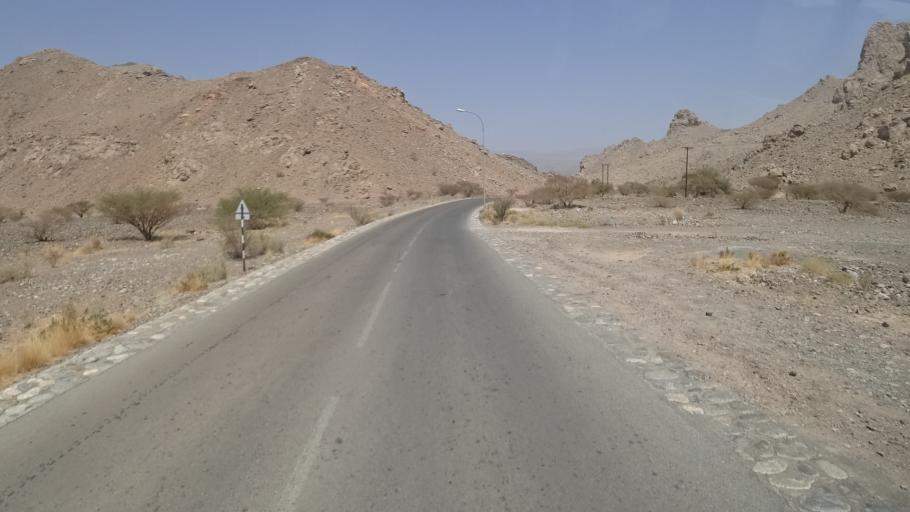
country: OM
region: Muhafazat ad Dakhiliyah
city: Bahla'
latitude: 23.0484
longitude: 57.3127
